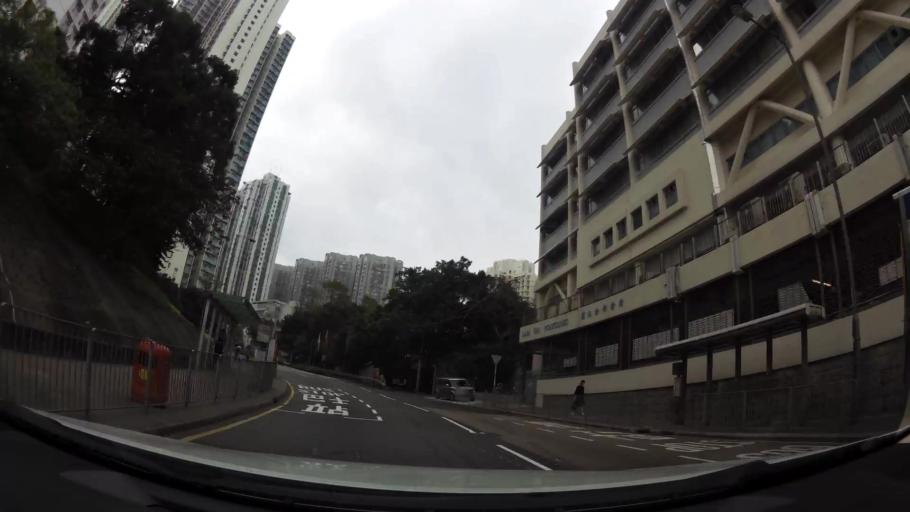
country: HK
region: Kowloon City
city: Kowloon
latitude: 22.3106
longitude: 114.2336
